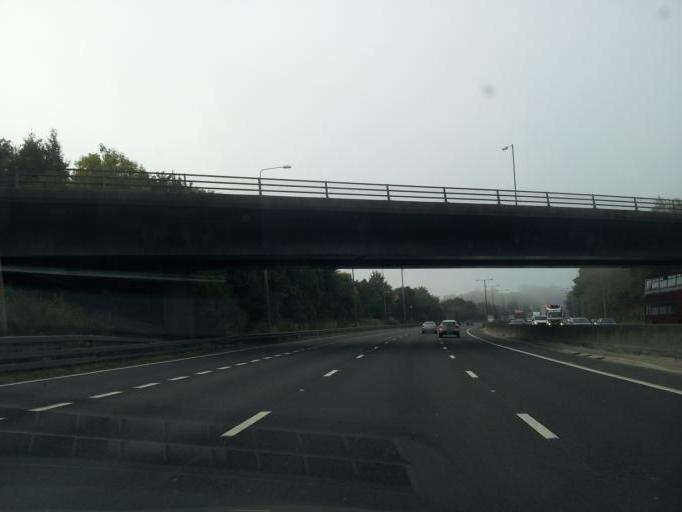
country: GB
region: England
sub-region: Kirklees
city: Cleckheaton
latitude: 53.7023
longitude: -1.7433
